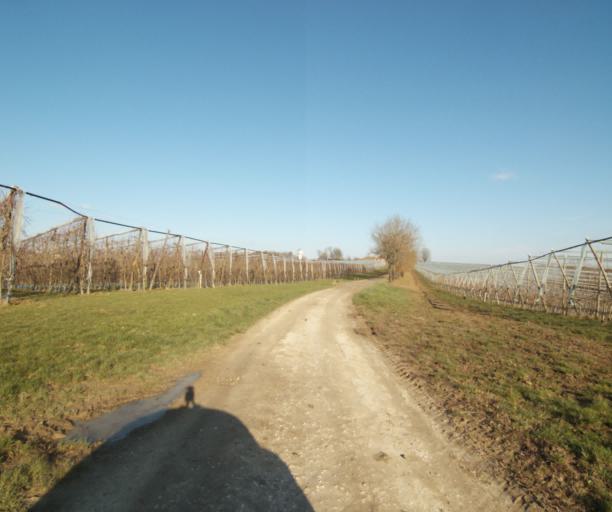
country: FR
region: Midi-Pyrenees
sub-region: Departement du Tarn-et-Garonne
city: Moissac
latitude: 44.1383
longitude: 1.0490
